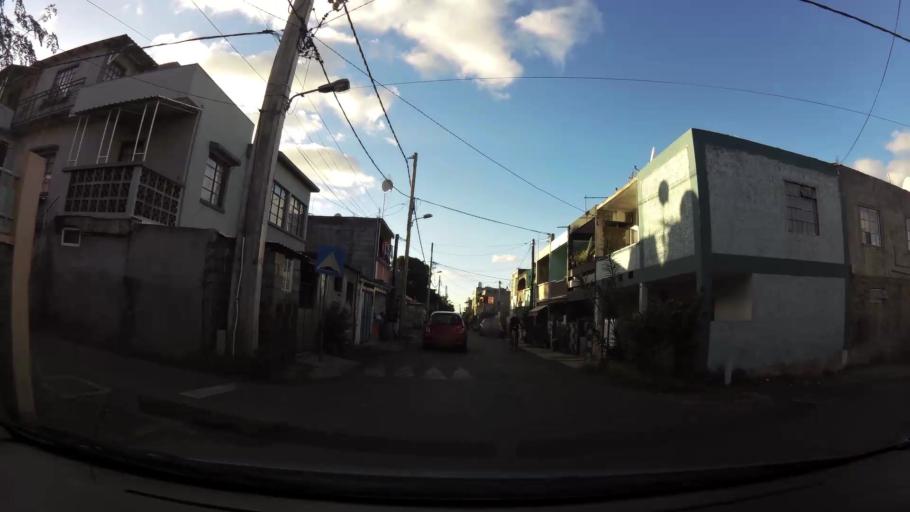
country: MU
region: Plaines Wilhems
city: Quatre Bornes
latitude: -20.2534
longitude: 57.4617
